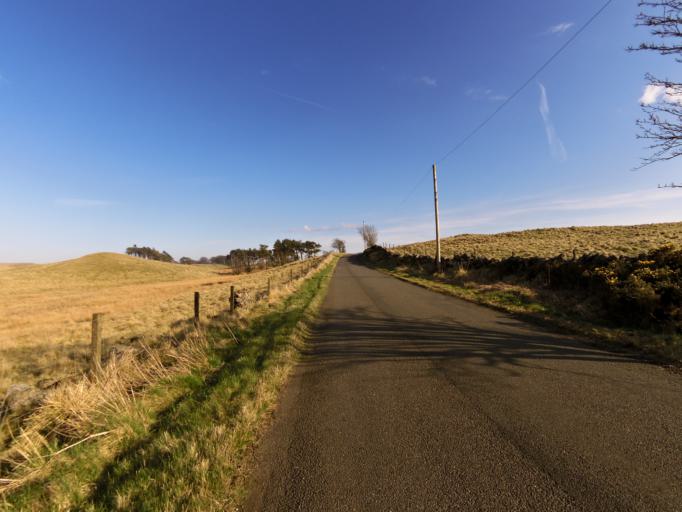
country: GB
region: Scotland
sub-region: Fife
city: Falkland
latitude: 56.2375
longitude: -3.2453
